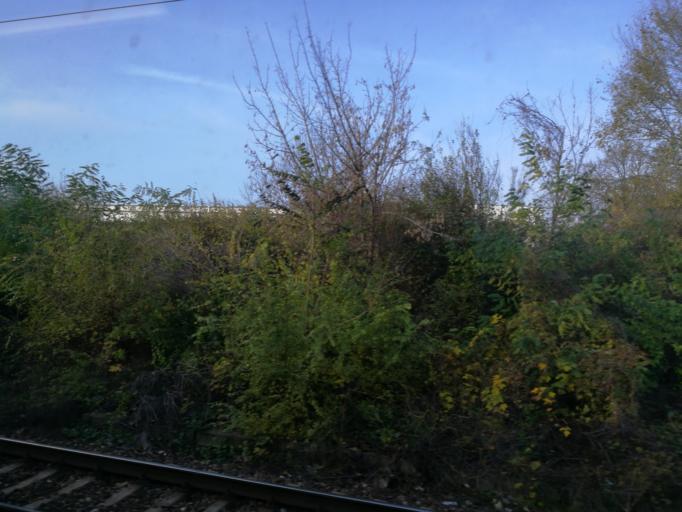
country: RO
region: Buzau
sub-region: Municipiul Ramnicu Sarat
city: Ramnicu Sarat
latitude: 45.3846
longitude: 27.0576
